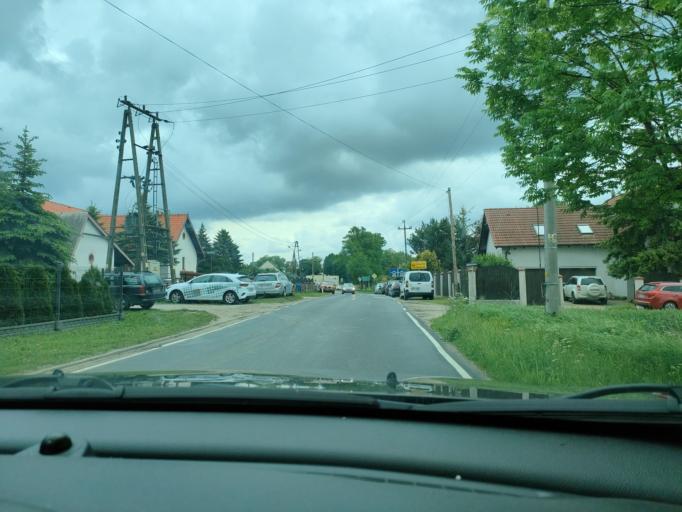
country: PL
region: Kujawsko-Pomorskie
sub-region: Bydgoszcz
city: Fordon
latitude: 53.2123
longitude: 18.1547
